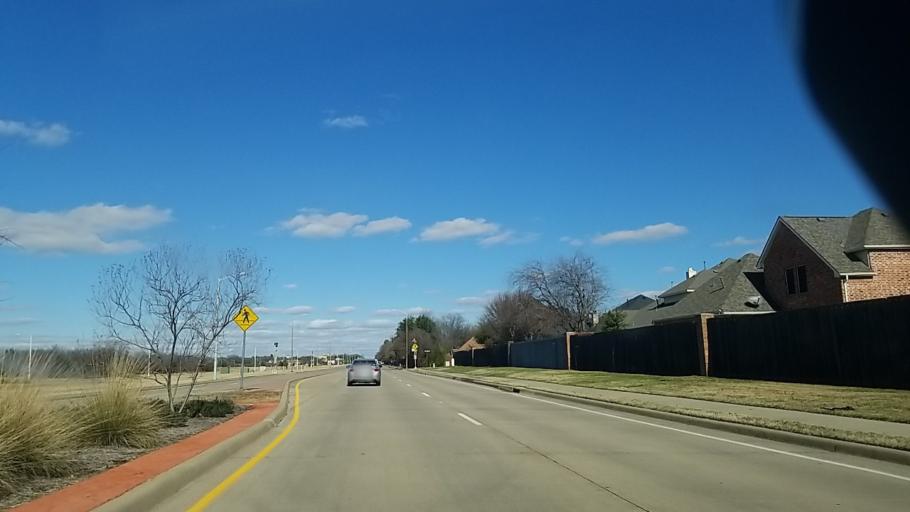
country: US
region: Texas
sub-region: Denton County
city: Denton
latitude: 33.1815
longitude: -97.1244
